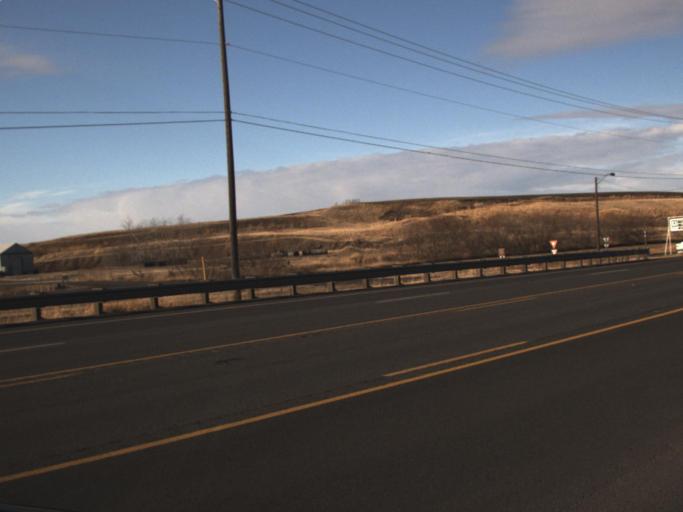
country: US
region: Idaho
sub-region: Latah County
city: Moscow
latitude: 46.7346
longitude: -117.0483
